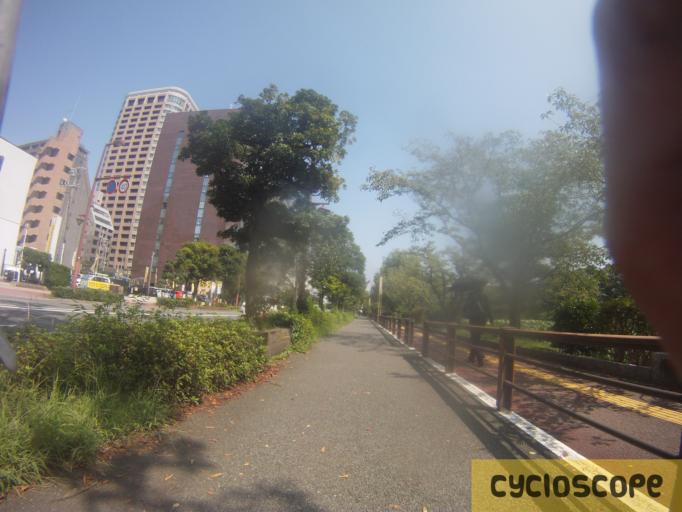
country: JP
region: Fukuoka
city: Fukuoka-shi
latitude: 33.5889
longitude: 130.3890
